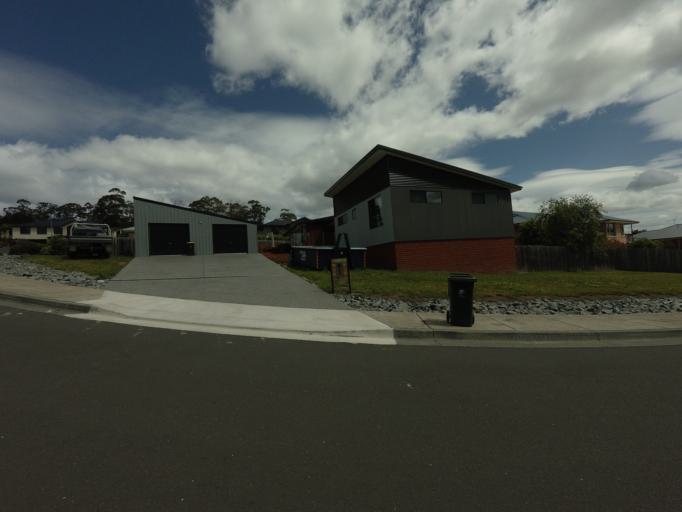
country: AU
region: Tasmania
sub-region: Clarence
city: Howrah
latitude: -42.8911
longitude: 147.4229
